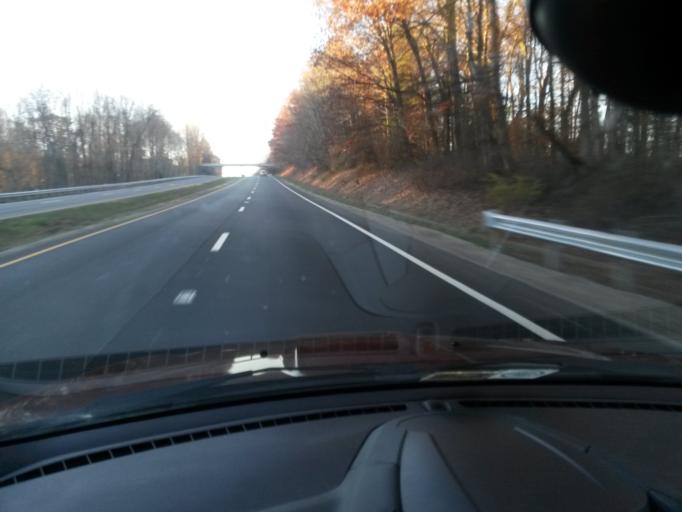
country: US
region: Virginia
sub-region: Franklin County
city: Henry Fork
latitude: 36.9856
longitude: -79.8712
